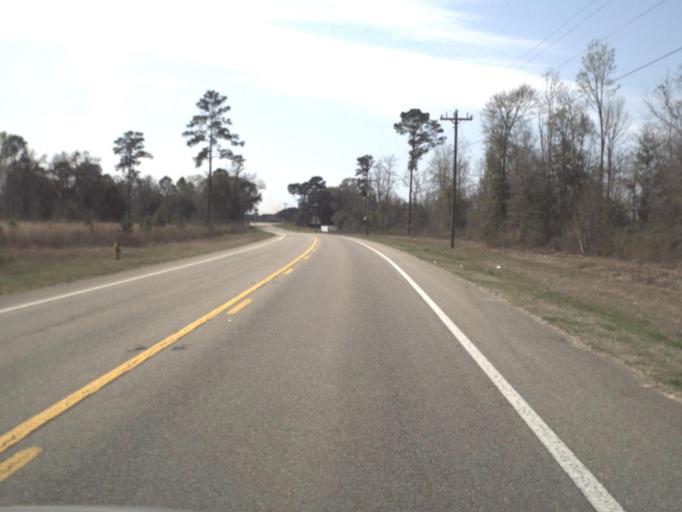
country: US
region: Florida
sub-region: Gadsden County
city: Gretna
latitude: 30.5871
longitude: -84.6925
